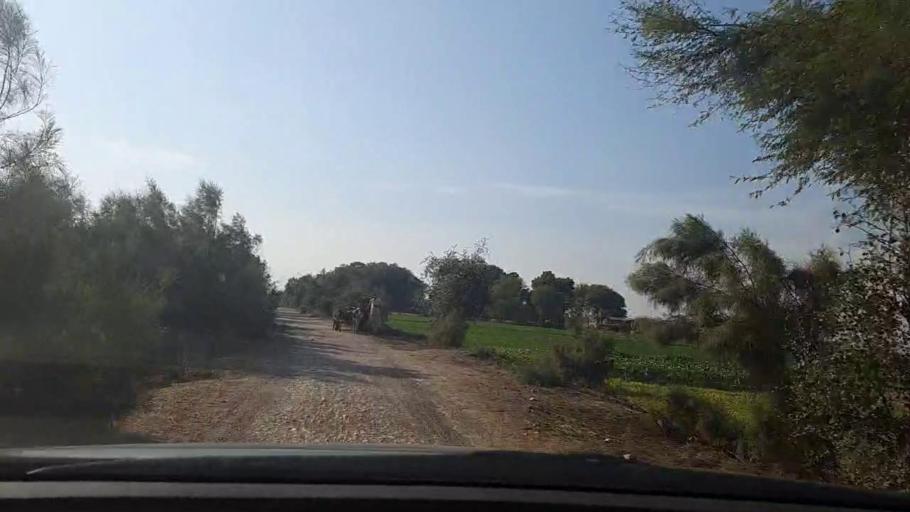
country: PK
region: Sindh
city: Sehwan
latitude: 26.3047
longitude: 67.9991
